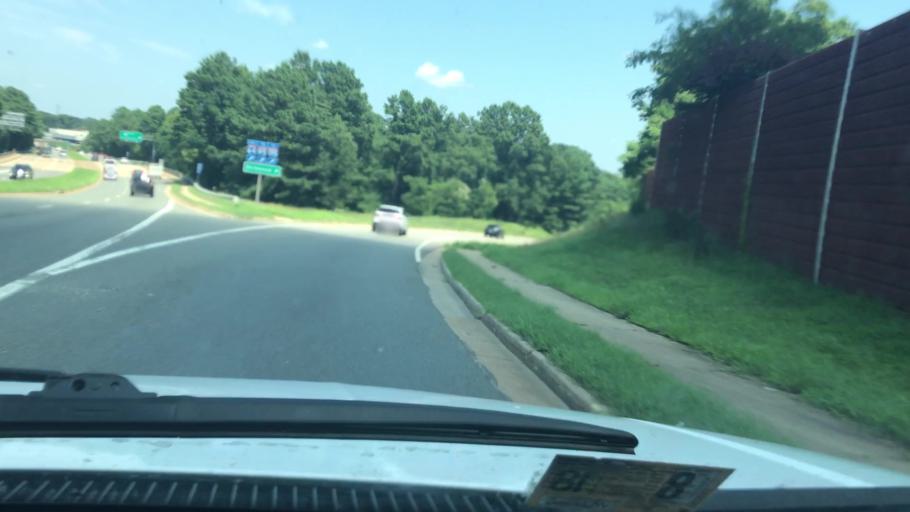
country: US
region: Virginia
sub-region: Henrico County
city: Dumbarton
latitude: 37.5956
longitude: -77.4918
